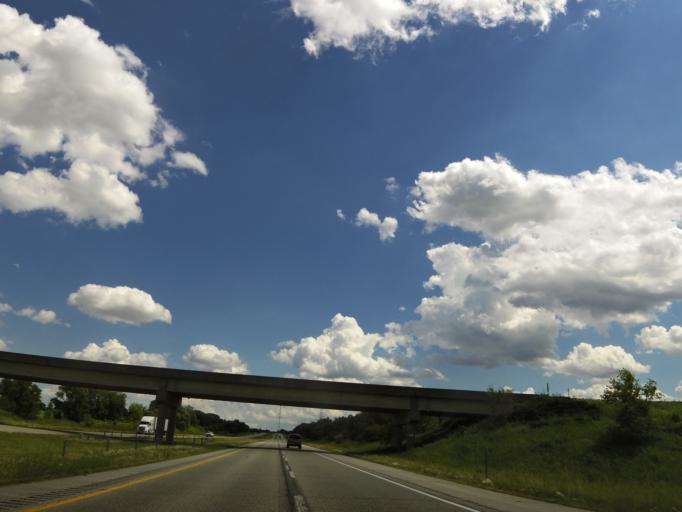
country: US
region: Iowa
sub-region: Linn County
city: Center Point
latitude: 42.1408
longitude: -91.7389
